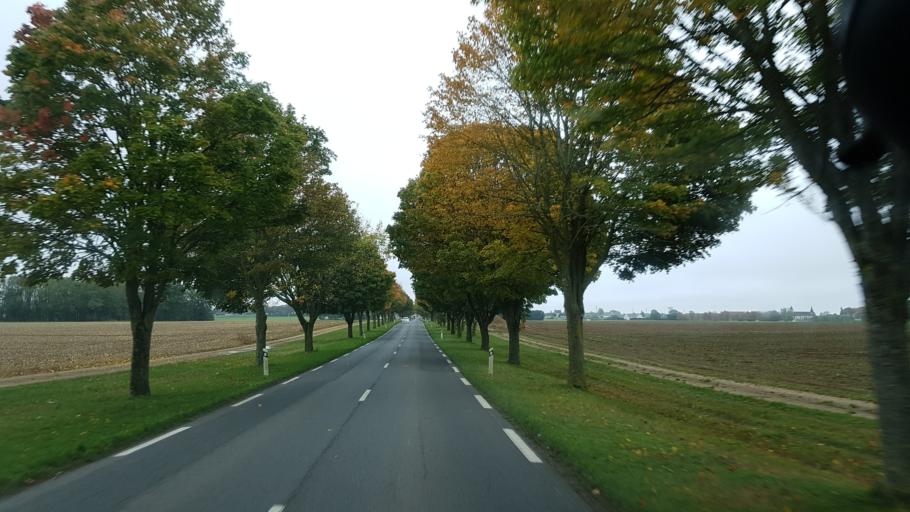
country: FR
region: Ile-de-France
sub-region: Departement de l'Essonne
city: Angerville
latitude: 48.3264
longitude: 1.9939
